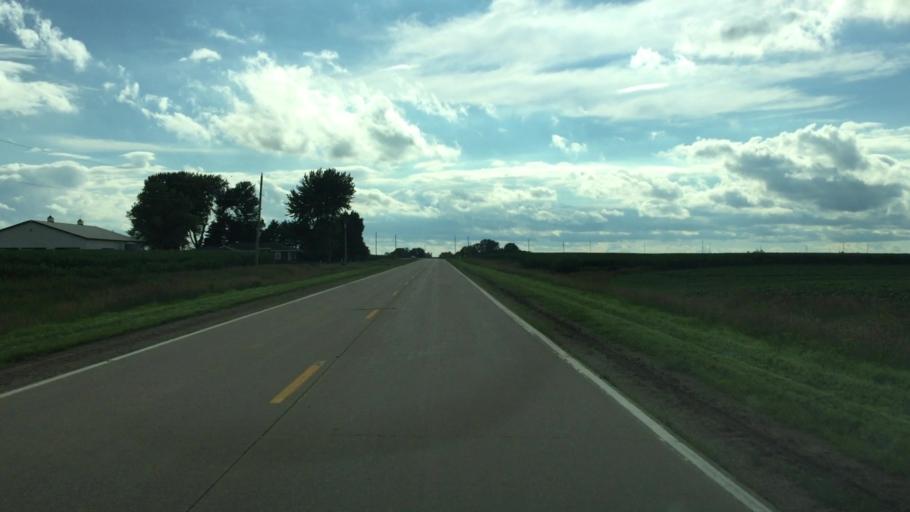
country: US
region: Iowa
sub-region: Jasper County
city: Prairie City
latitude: 41.5806
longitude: -93.1726
